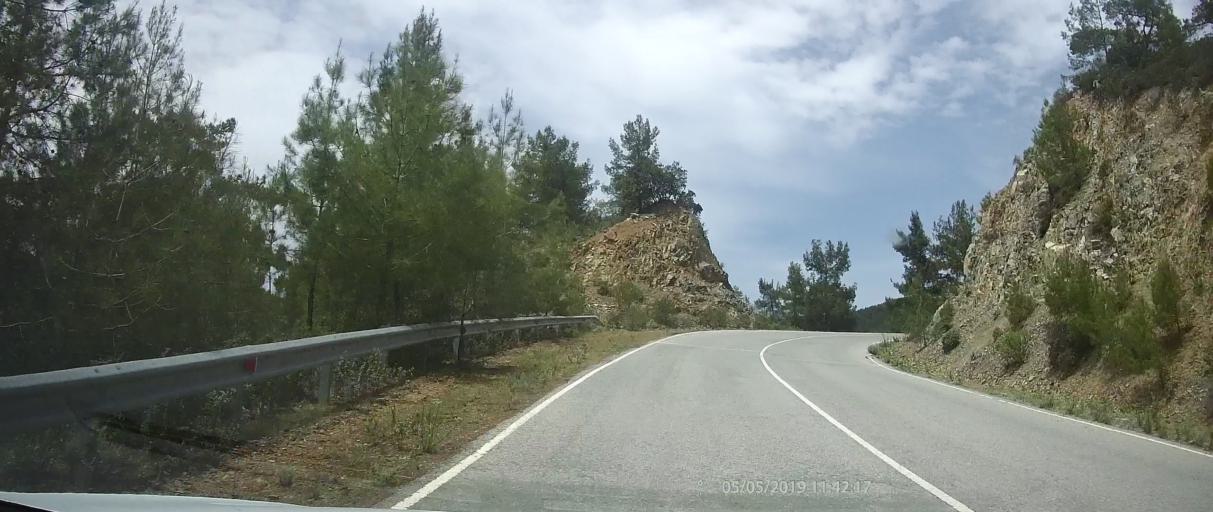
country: CY
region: Lefkosia
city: Kato Pyrgos
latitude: 35.0011
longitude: 32.6712
